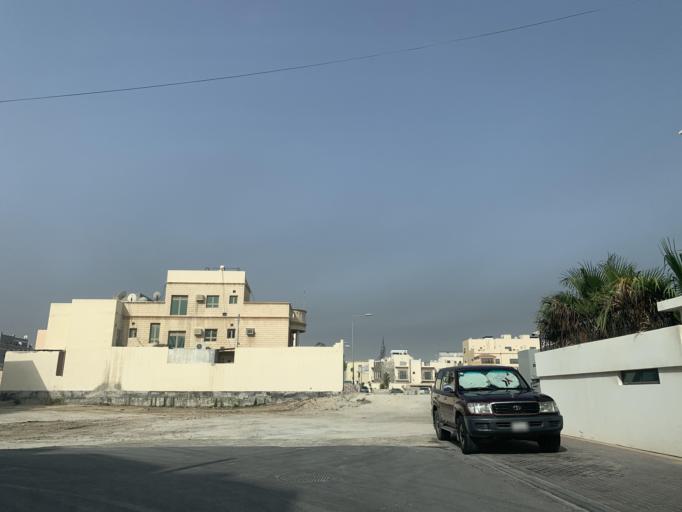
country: BH
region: Northern
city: Madinat `Isa
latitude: 26.1891
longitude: 50.5599
